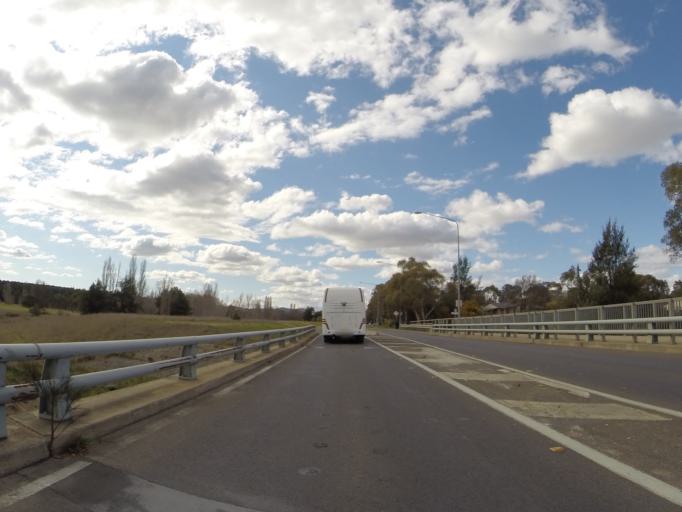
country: AU
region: Australian Capital Territory
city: Belconnen
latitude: -35.2127
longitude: 149.0871
